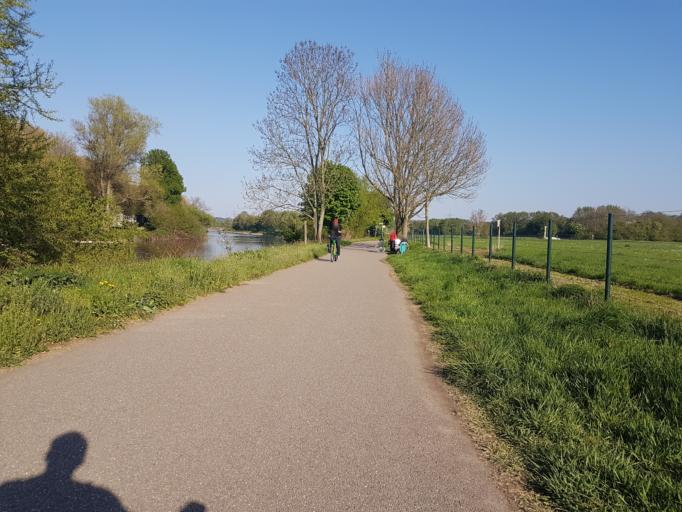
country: DE
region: North Rhine-Westphalia
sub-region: Regierungsbezirk Munster
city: Gelsenkirchen
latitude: 51.4287
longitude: 7.0984
